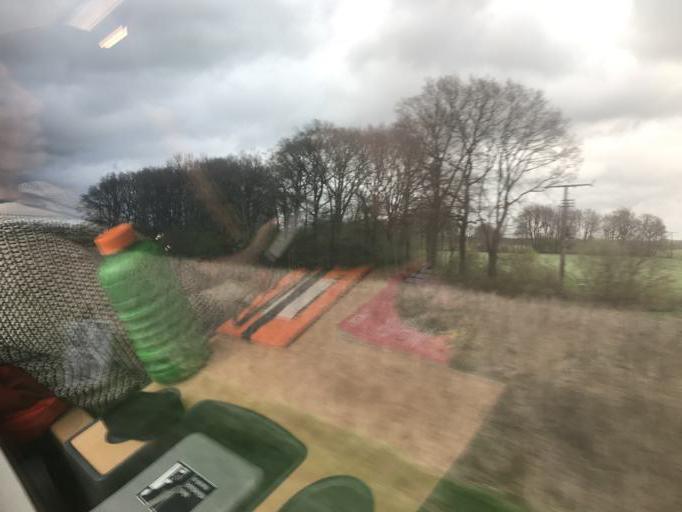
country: DE
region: Schleswig-Holstein
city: Wulfsmoor
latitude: 53.8914
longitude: 9.7133
